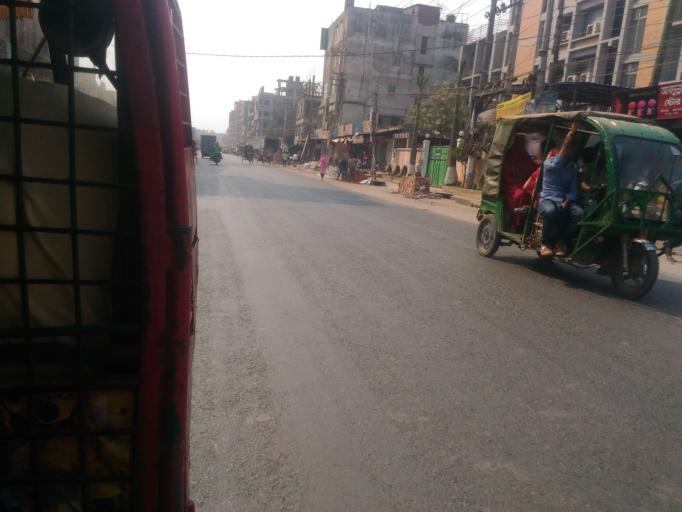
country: BD
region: Dhaka
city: Tungi
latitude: 23.9908
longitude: 90.3893
